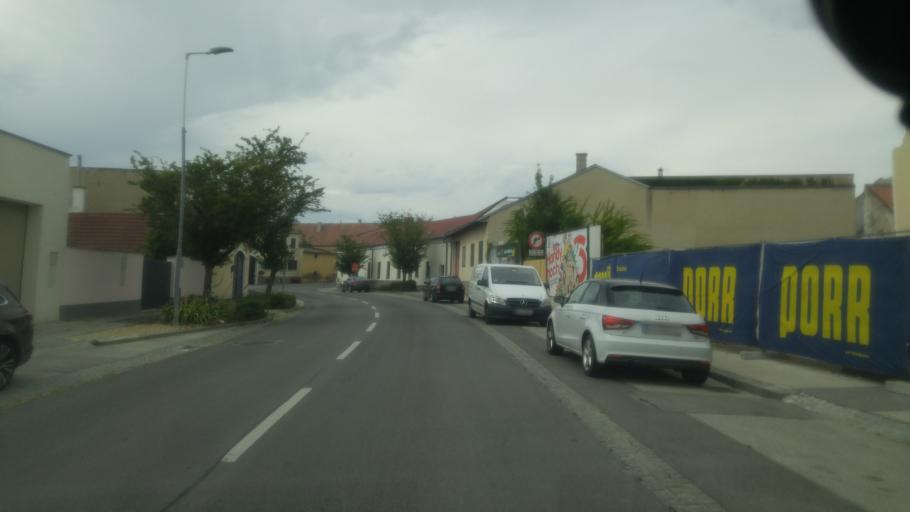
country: AT
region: Lower Austria
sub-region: Politischer Bezirk Wien-Umgebung
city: Moosbrunn
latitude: 48.0405
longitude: 16.4450
